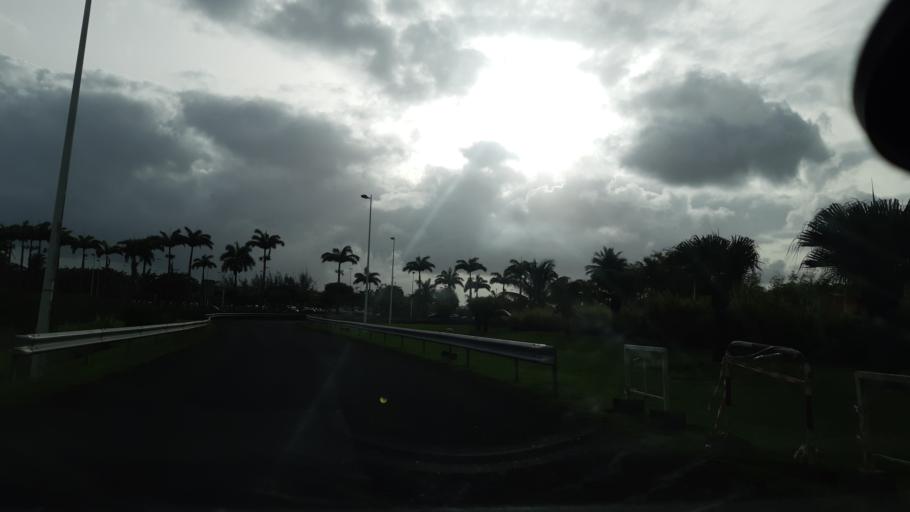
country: GP
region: Guadeloupe
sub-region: Guadeloupe
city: Les Abymes
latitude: 16.2717
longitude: -61.5235
